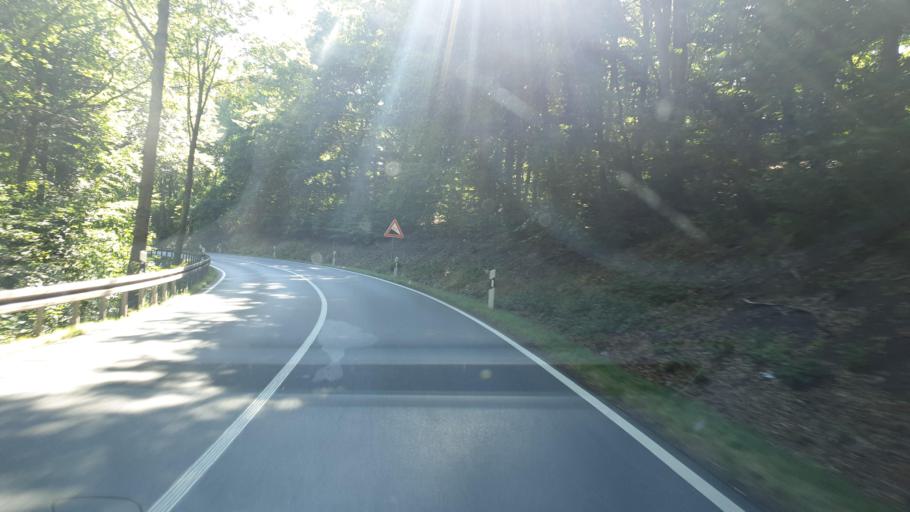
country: DE
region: Saxony
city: Aue
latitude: 50.5873
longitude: 12.7279
